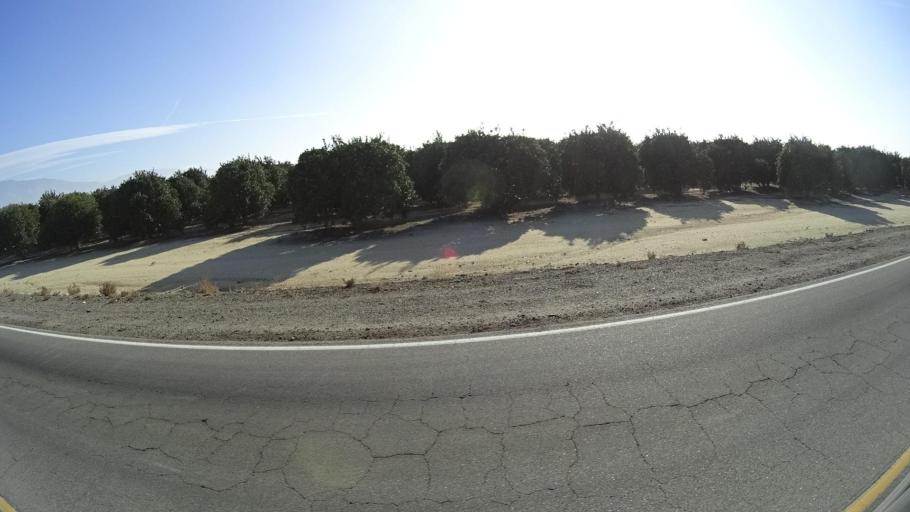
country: US
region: California
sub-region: Kern County
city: Arvin
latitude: 35.3268
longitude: -118.7838
